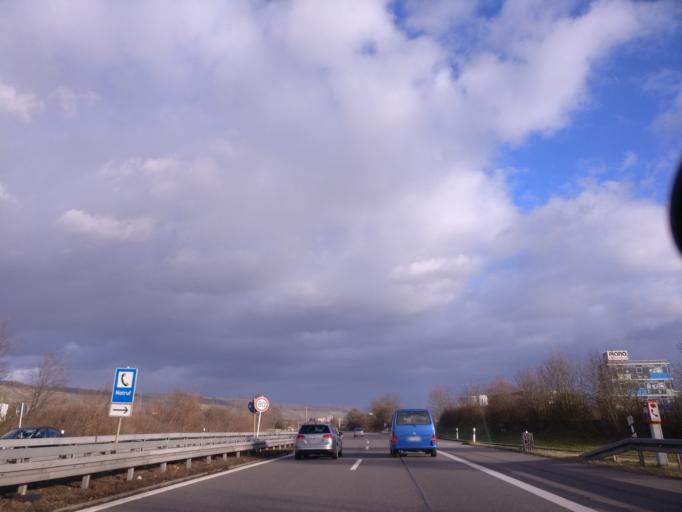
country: DE
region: Baden-Wuerttemberg
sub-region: Regierungsbezirk Stuttgart
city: Weinstadt-Endersbach
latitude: 48.8139
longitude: 9.3494
